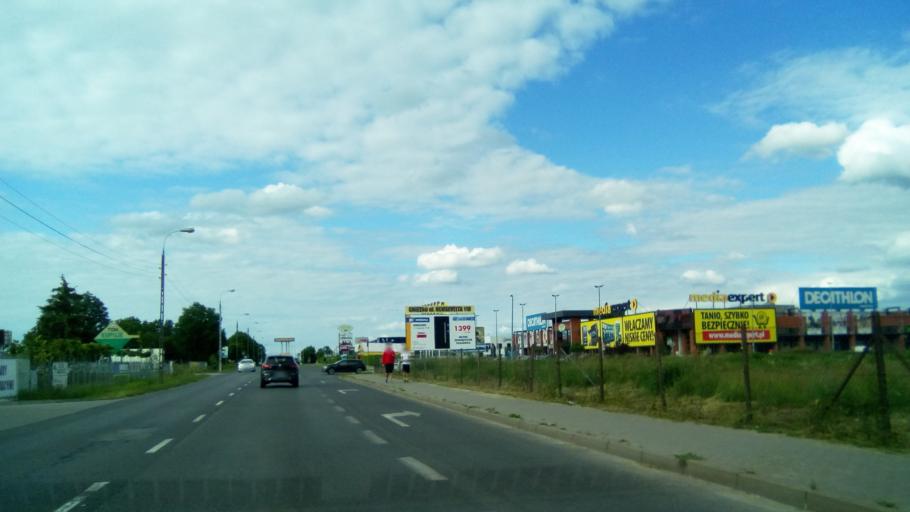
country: PL
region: Greater Poland Voivodeship
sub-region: Powiat gnieznienski
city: Gniezno
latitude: 52.5581
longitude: 17.6079
